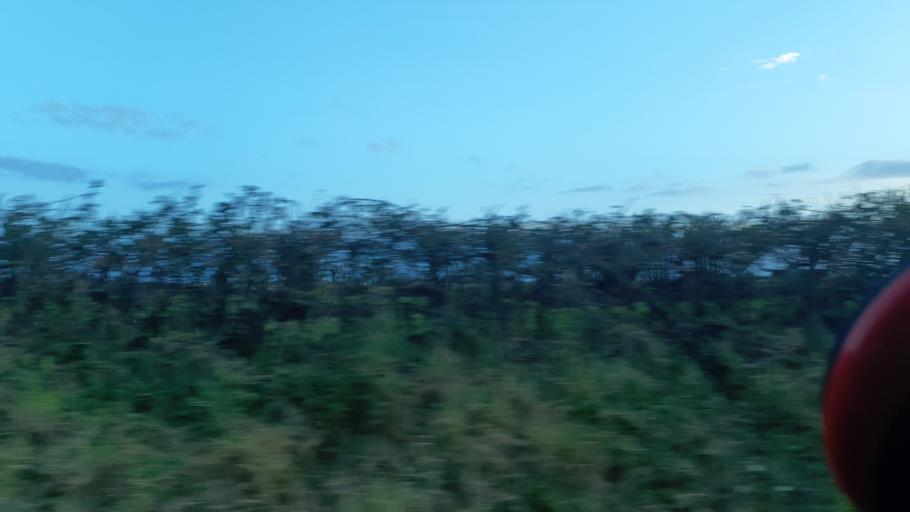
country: GB
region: Northern Ireland
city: Kilkeel
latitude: 54.0407
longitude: -6.0752
